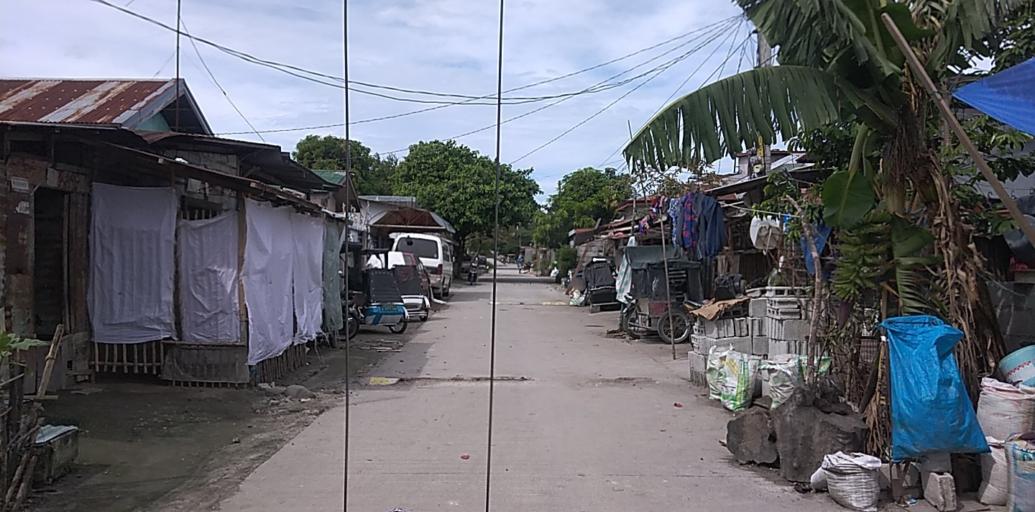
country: PH
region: Central Luzon
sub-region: Province of Pampanga
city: Manibaug Pasig
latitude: 15.1132
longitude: 120.5592
